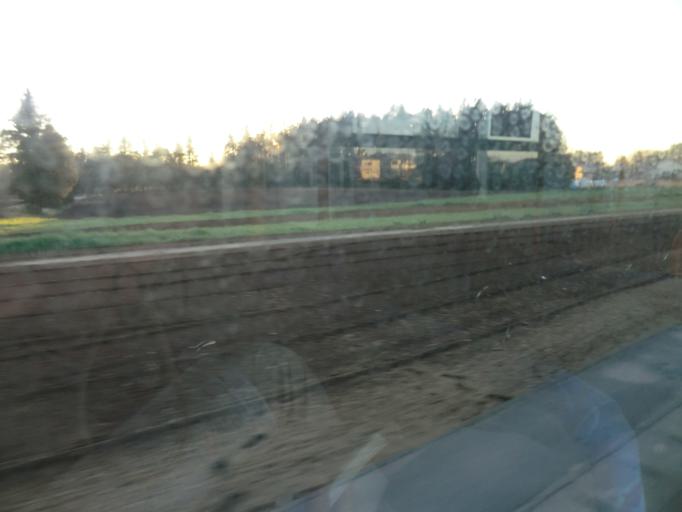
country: JP
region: Ibaraki
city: Ushiku
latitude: 35.9969
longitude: 140.1283
